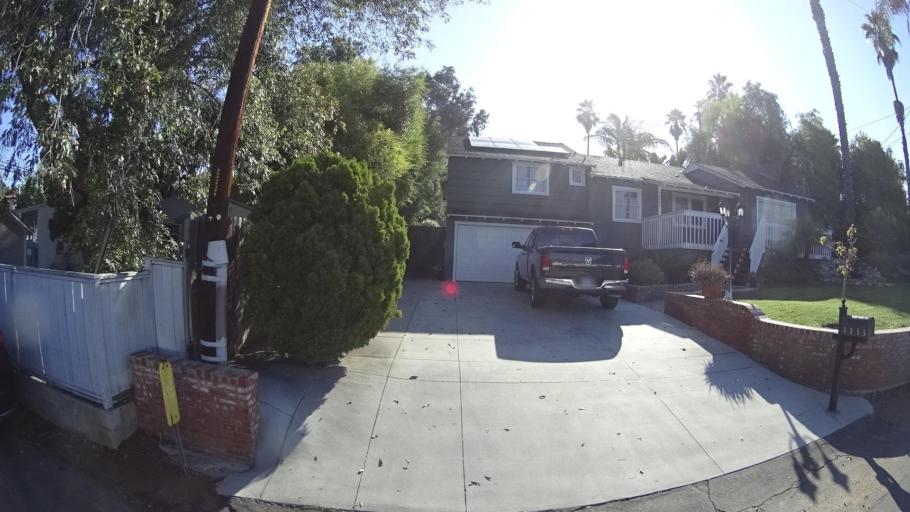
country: US
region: California
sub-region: San Diego County
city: Spring Valley
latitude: 32.7678
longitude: -116.9979
